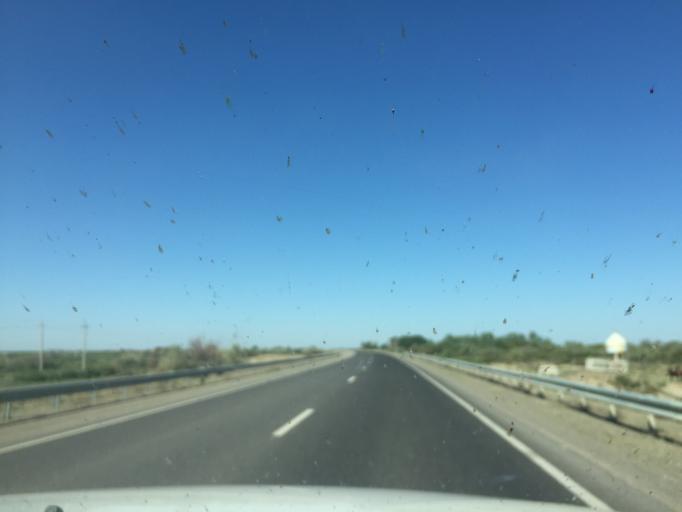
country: KZ
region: Qyzylorda
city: Terenozek
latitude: 44.8838
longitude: 64.8981
